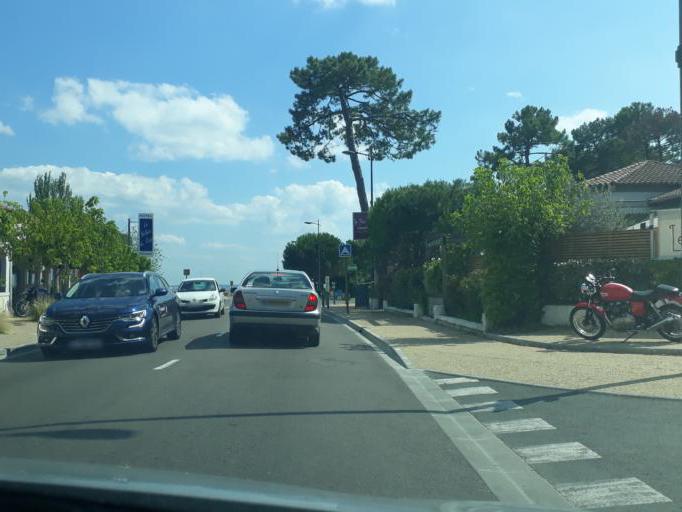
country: FR
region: Aquitaine
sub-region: Departement de la Gironde
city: Ares
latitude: 44.7452
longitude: -1.1814
